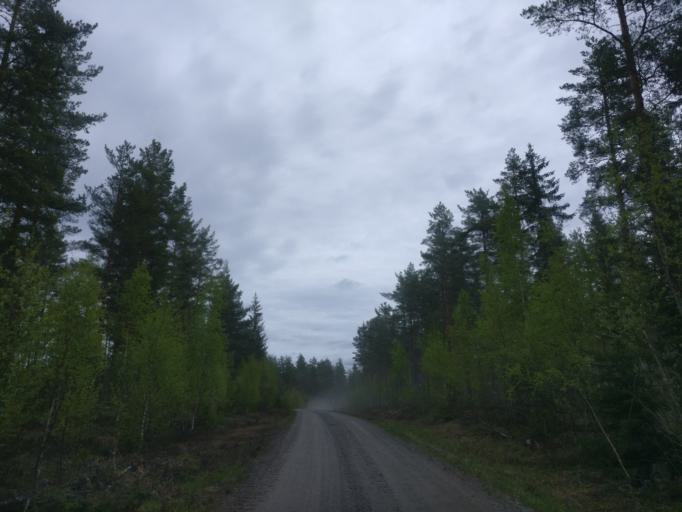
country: SE
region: Gaevleborg
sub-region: Soderhamns Kommun
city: Soderhamn
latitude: 61.4207
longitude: 16.9047
